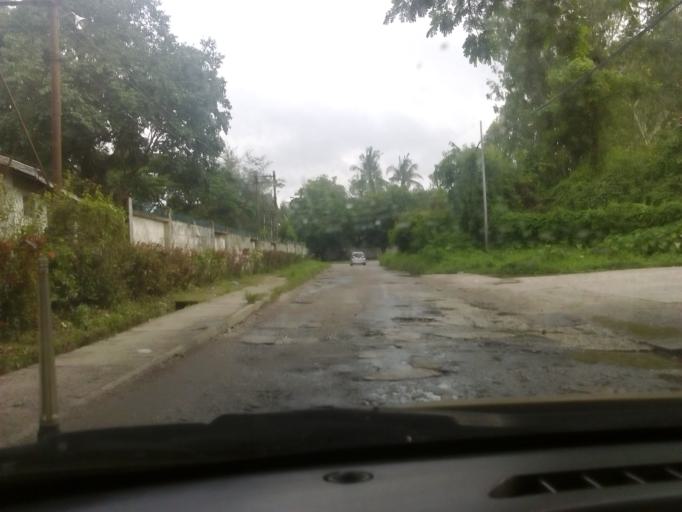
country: MM
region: Yangon
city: Yangon
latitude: 16.8440
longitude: 96.1525
